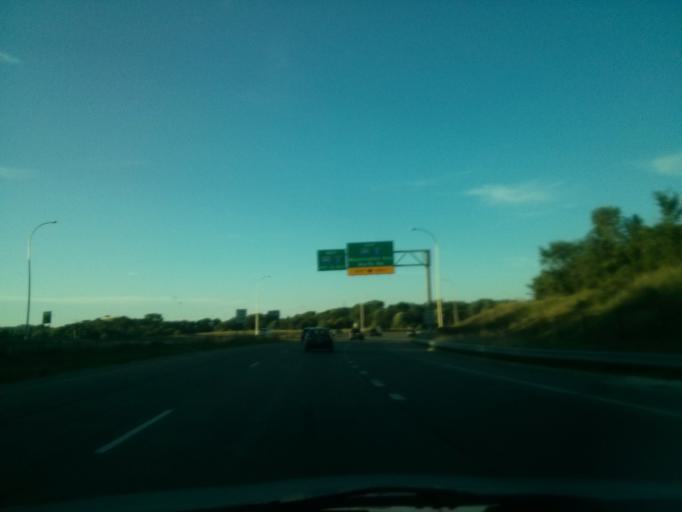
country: US
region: Minnesota
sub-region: Hennepin County
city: Edina
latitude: 44.8493
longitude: -93.3982
